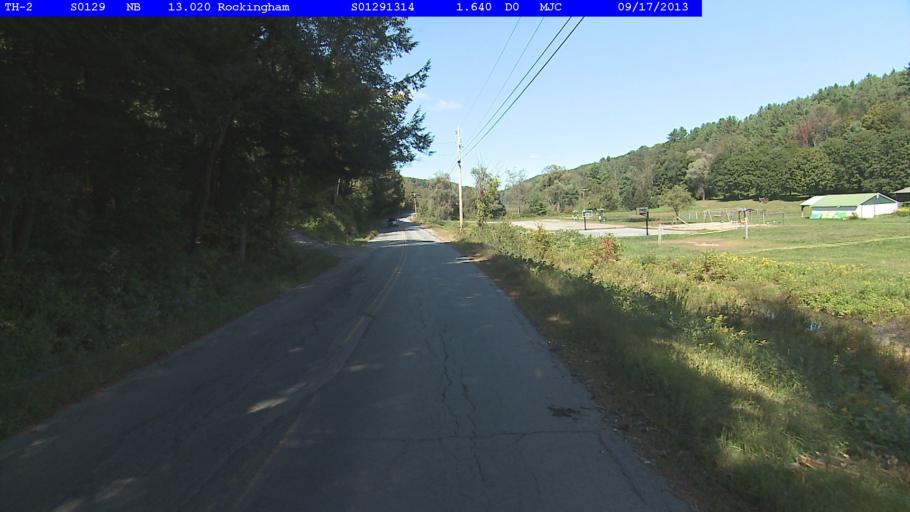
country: US
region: Vermont
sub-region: Windham County
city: Rockingham
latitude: 43.1411
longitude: -72.5177
